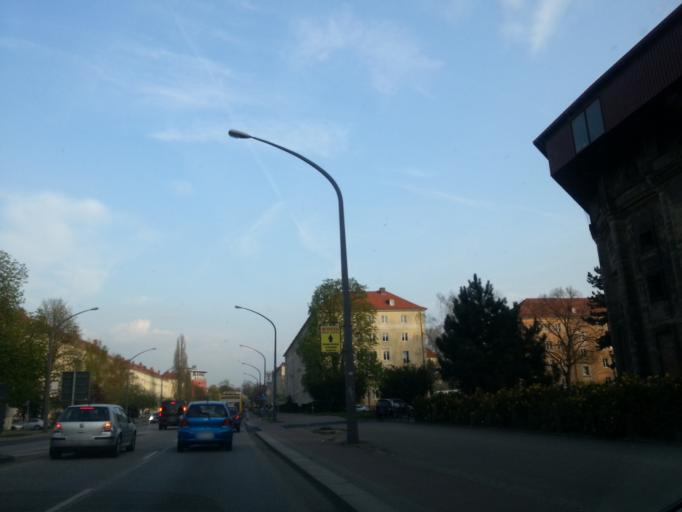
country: DE
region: Saxony
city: Dresden
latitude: 51.0362
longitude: 13.7171
